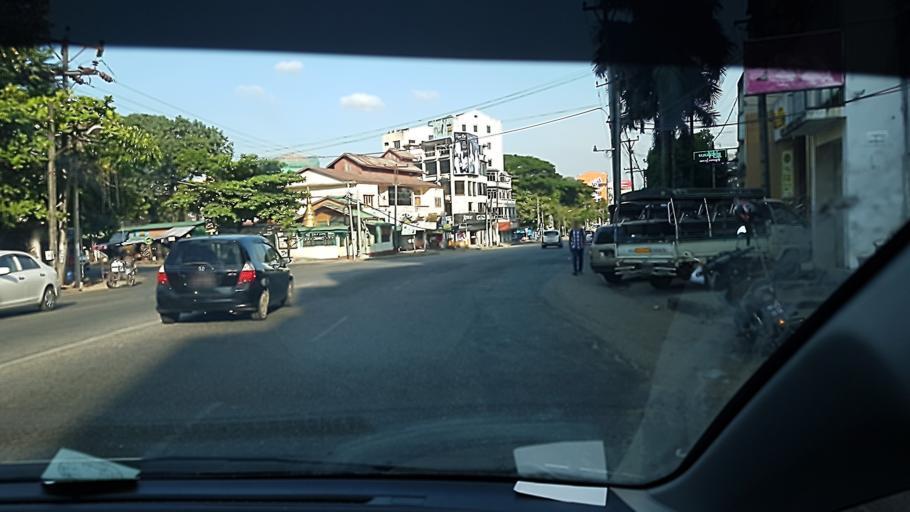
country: MM
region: Yangon
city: Yangon
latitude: 16.8117
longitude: 96.1671
